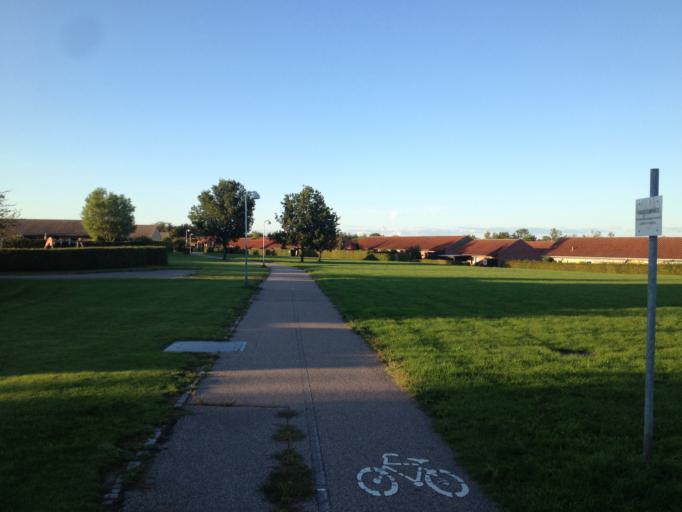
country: DK
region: Capital Region
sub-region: Fredensborg Kommune
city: Niva
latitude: 55.9430
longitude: 12.5052
